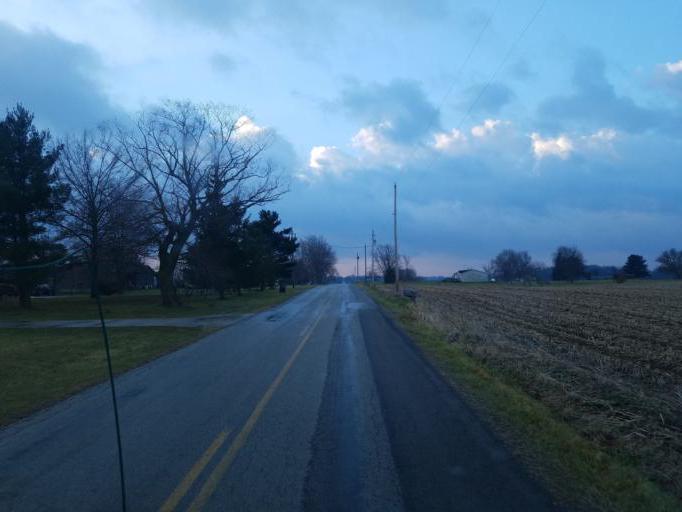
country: US
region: Ohio
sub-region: Marion County
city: Marion
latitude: 40.6329
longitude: -83.1886
